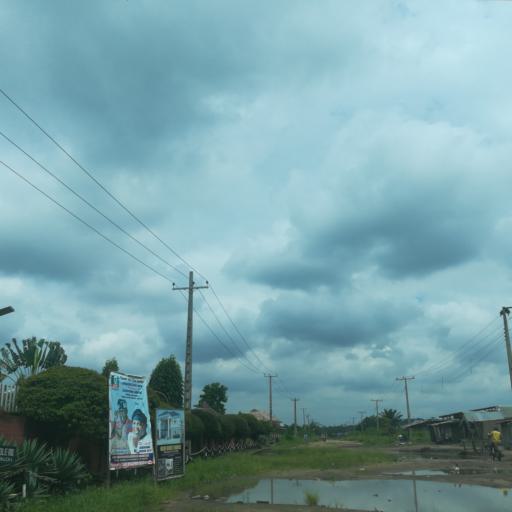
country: NG
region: Lagos
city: Ejirin
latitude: 6.6258
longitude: 3.7061
